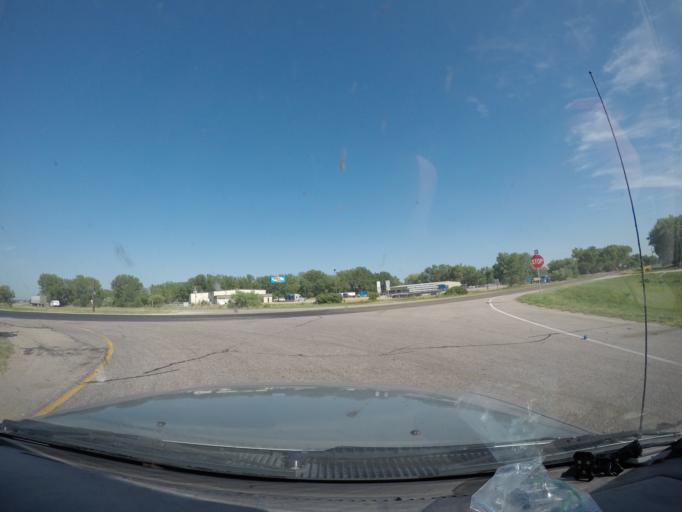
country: US
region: Nebraska
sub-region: Buffalo County
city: Kearney
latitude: 40.6742
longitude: -99.2559
